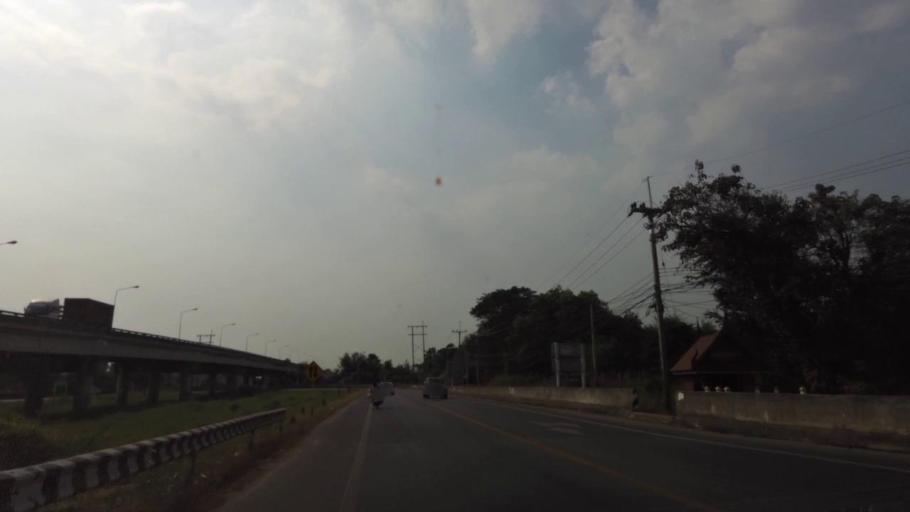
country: TH
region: Phra Nakhon Si Ayutthaya
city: Phra Nakhon Si Ayutthaya
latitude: 14.3049
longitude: 100.5693
